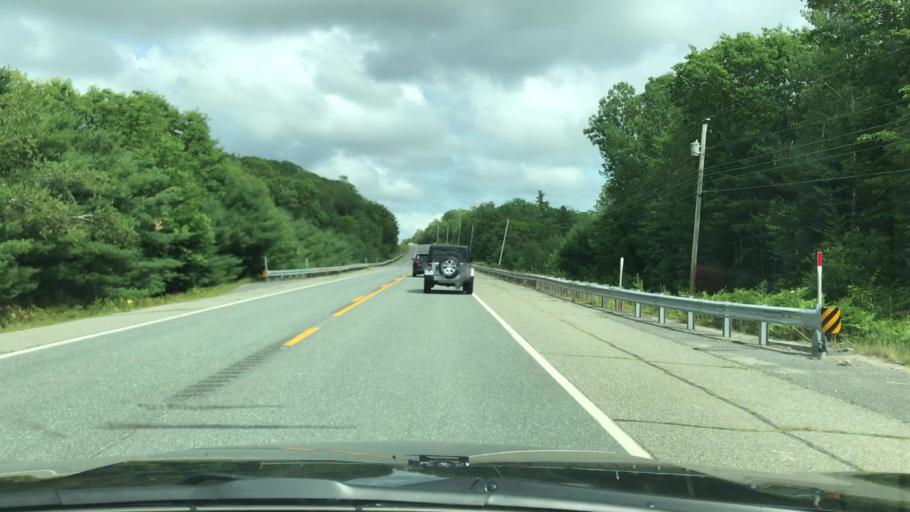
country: US
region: Maine
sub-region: Hancock County
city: Surry
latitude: 44.5652
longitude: -68.6065
